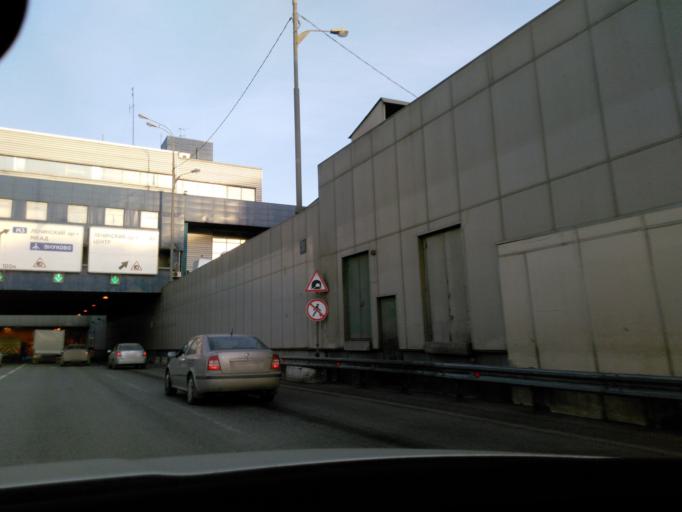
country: RU
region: Moscow
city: Novyye Cheremushki
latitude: 55.7063
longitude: 37.5905
